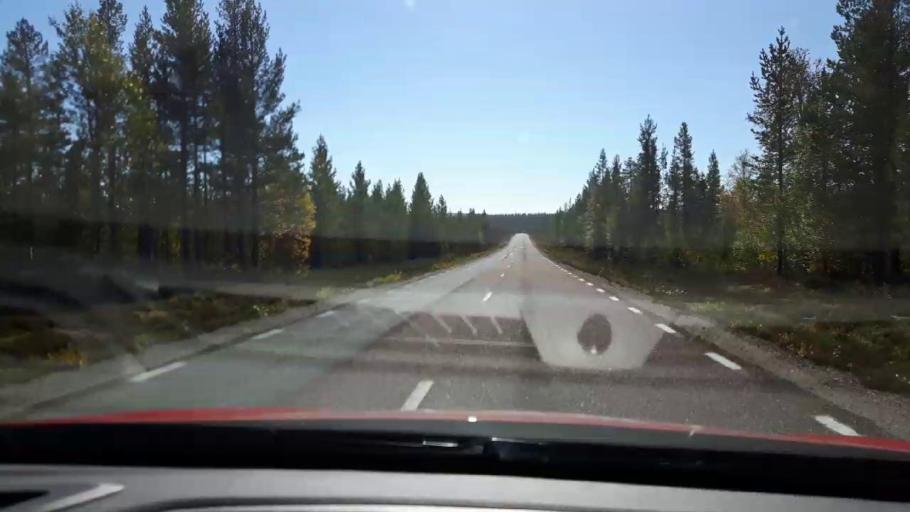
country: SE
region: Jaemtland
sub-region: Harjedalens Kommun
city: Sveg
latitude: 61.7182
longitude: 14.1682
